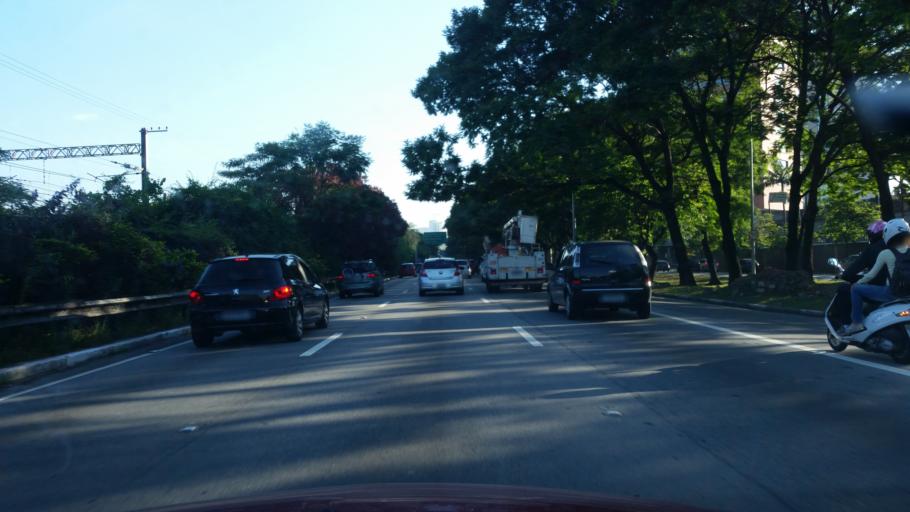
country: BR
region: Sao Paulo
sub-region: Taboao Da Serra
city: Taboao da Serra
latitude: -23.6321
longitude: -46.7160
